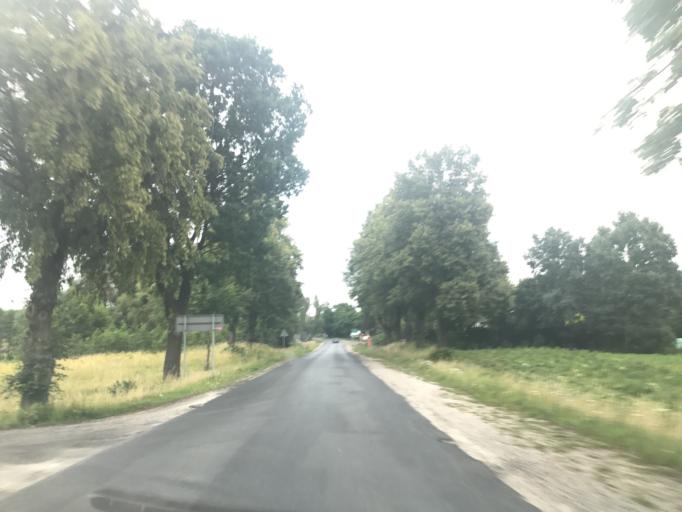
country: PL
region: Kujawsko-Pomorskie
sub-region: Powiat lipnowski
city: Lipno
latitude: 52.8330
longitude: 19.1846
